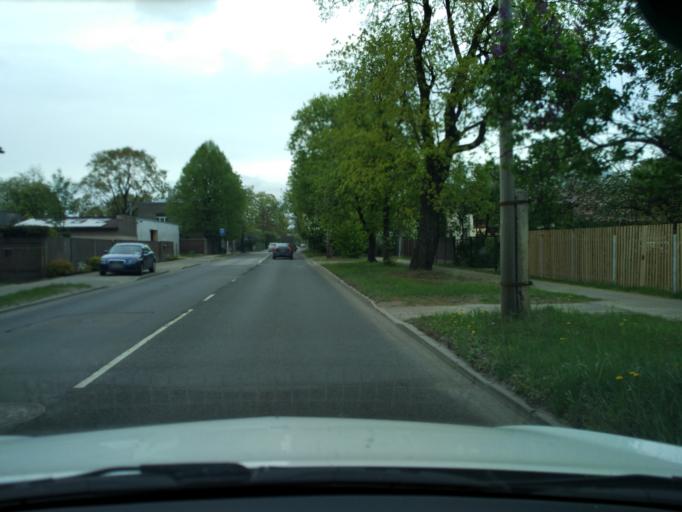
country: LV
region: Marupe
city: Marupe
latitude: 56.9181
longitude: 24.0743
